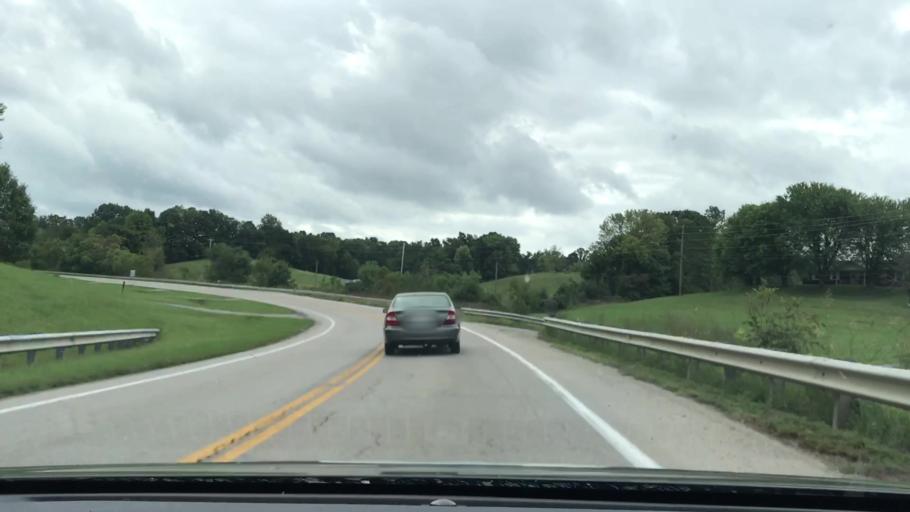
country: US
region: Kentucky
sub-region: Barren County
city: Glasgow
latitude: 36.9117
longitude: -85.7849
